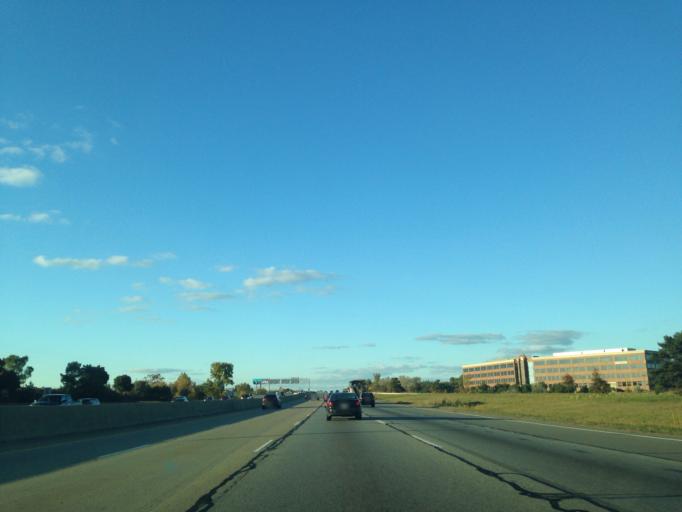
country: US
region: Michigan
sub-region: Oakland County
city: Auburn Hills
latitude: 42.6660
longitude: -83.2411
